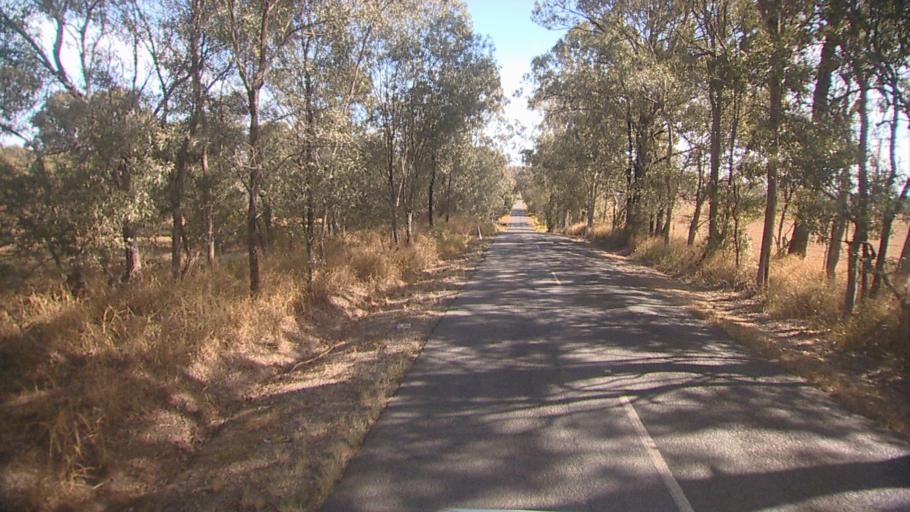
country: AU
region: Queensland
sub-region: Logan
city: Cedar Vale
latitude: -27.8676
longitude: 153.0162
